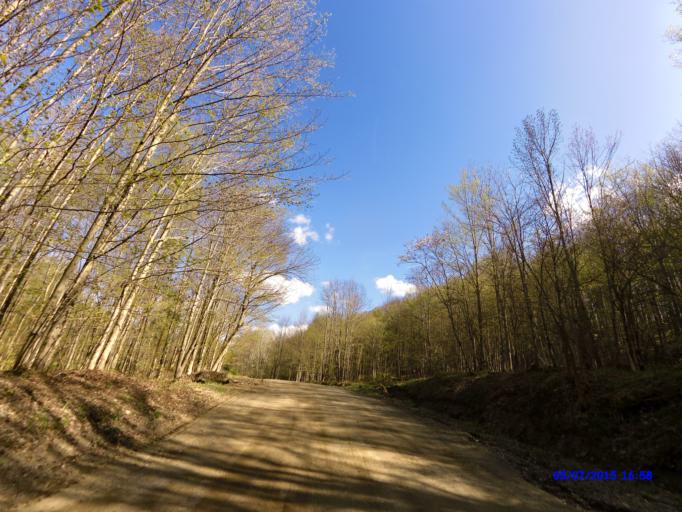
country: US
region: New York
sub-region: Cattaraugus County
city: Little Valley
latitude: 42.2924
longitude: -78.7466
